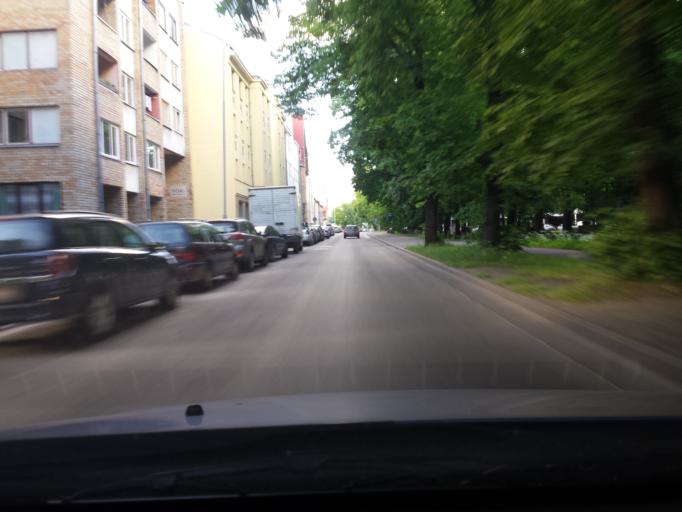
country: LV
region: Riga
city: Riga
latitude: 56.9738
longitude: 24.1438
